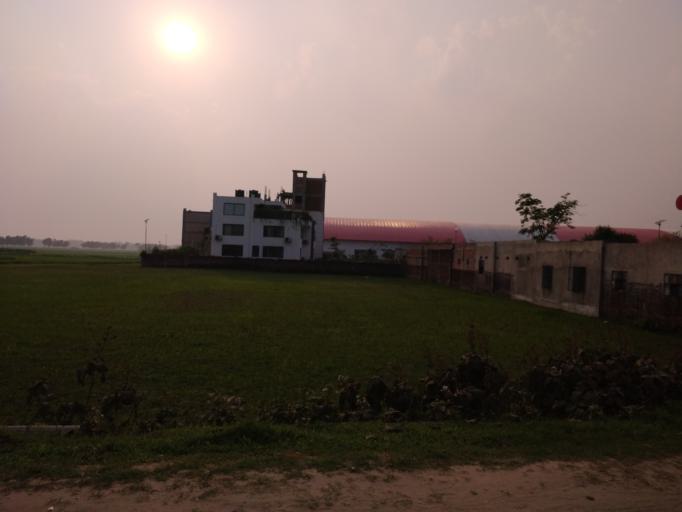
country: IN
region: Tripura
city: Khowai
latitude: 24.1338
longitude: 91.3519
